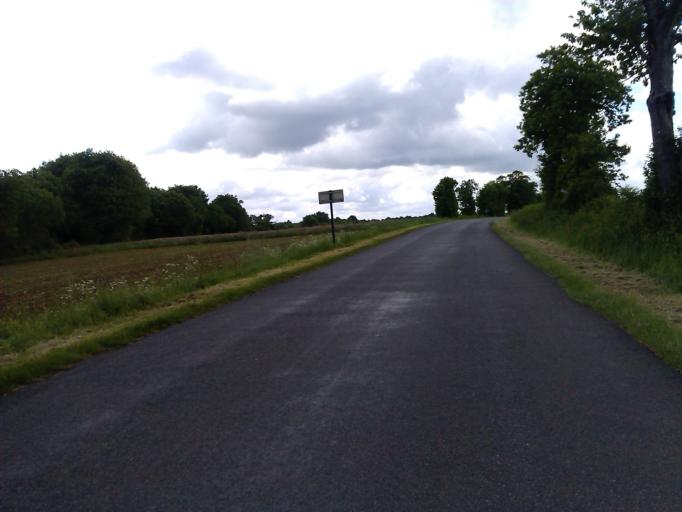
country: FR
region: Poitou-Charentes
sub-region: Departement de la Charente
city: Champagne-Mouton
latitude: 46.0210
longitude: 0.4393
